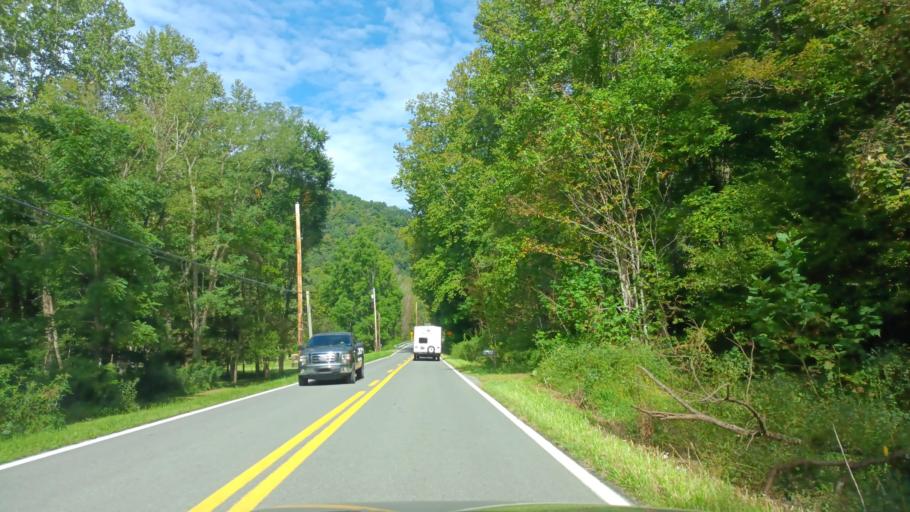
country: US
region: West Virginia
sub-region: Preston County
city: Terra Alta
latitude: 39.2955
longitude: -79.6377
